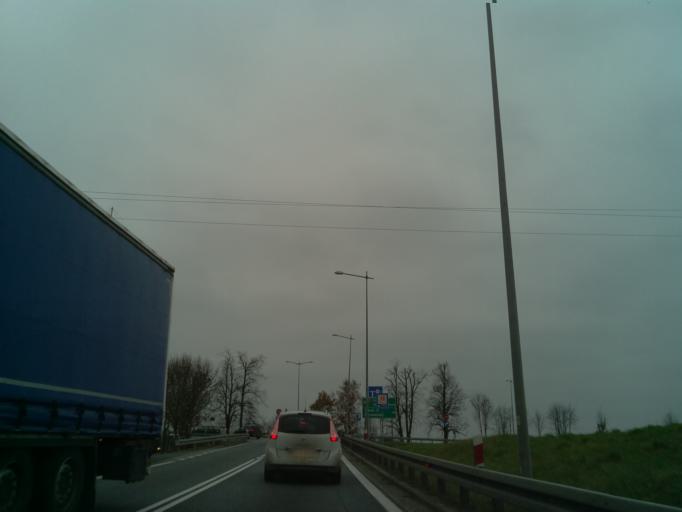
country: PL
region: Lower Silesian Voivodeship
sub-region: Powiat sredzki
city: Ciechow
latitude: 51.0429
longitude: 16.5969
